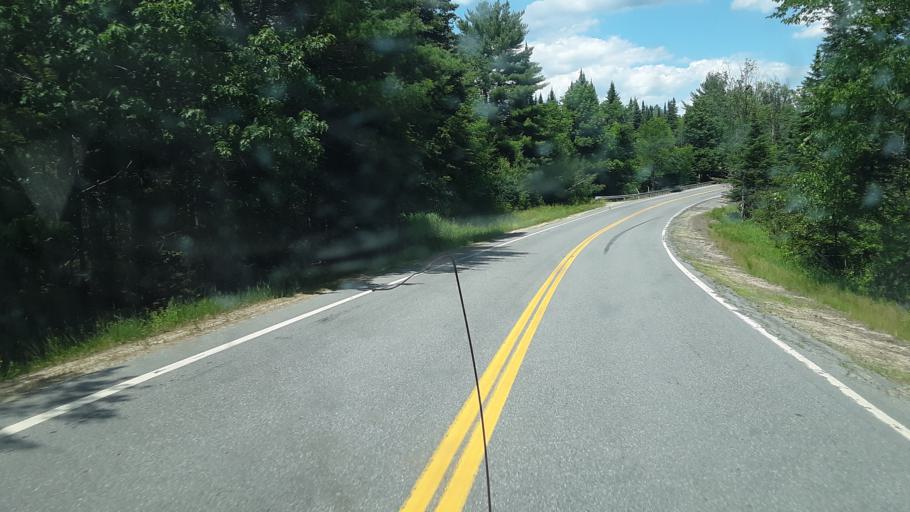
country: US
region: Maine
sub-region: Franklin County
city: Chesterville
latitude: 44.5868
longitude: -70.1505
